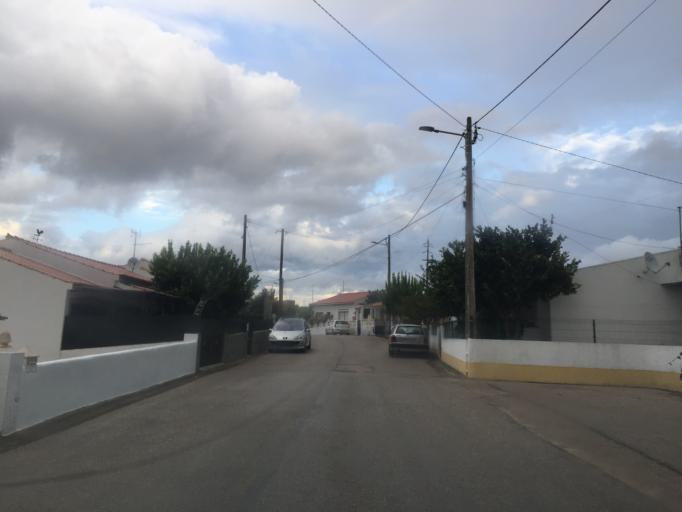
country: PT
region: Portalegre
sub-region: Marvao
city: Marvao
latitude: 39.4108
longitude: -7.3496
